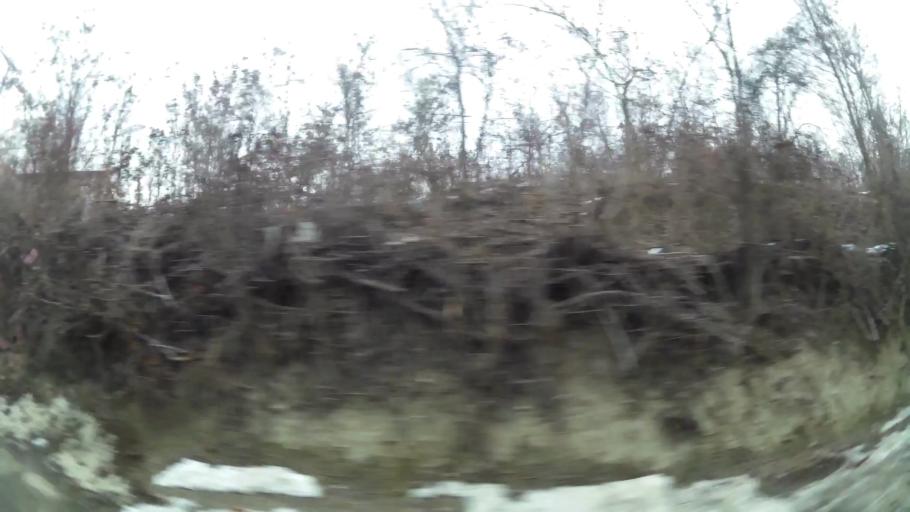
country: MK
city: Kondovo
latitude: 42.0108
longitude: 21.3182
